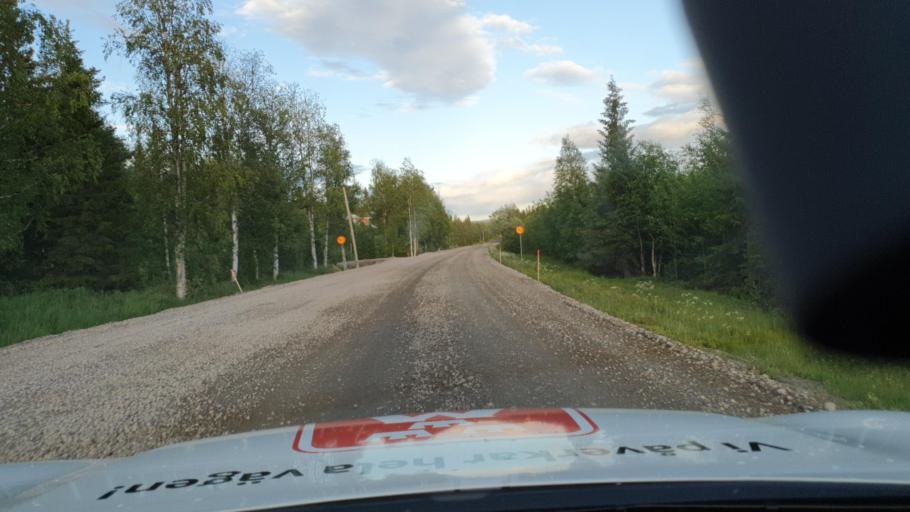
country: SE
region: Vaesterbotten
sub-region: Lycksele Kommun
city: Soderfors
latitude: 64.6805
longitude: 17.8196
